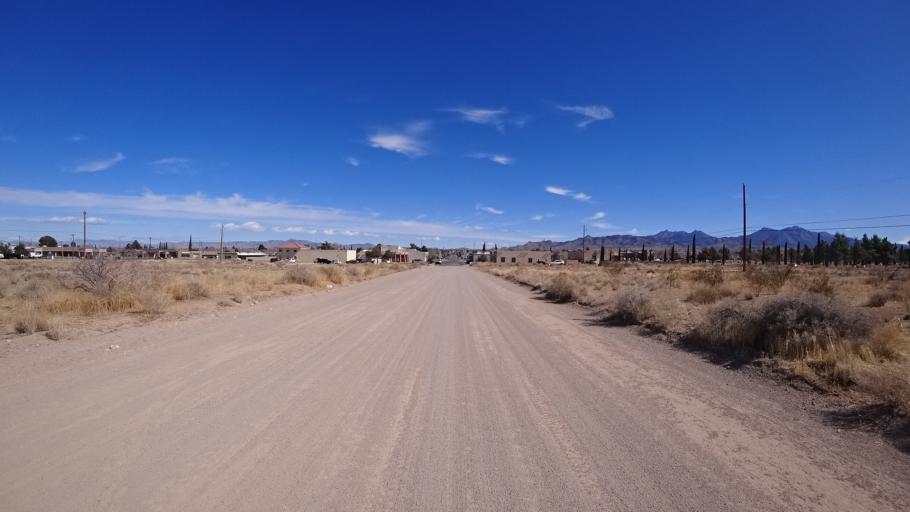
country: US
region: Arizona
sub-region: Mohave County
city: Kingman
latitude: 35.2039
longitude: -114.0359
